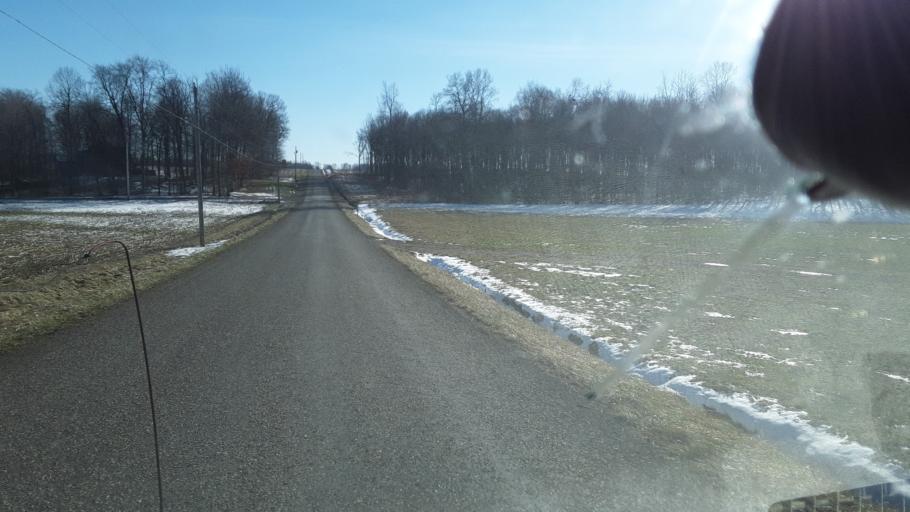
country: US
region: Ohio
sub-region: Ashland County
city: Loudonville
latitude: 40.7346
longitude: -82.2220
